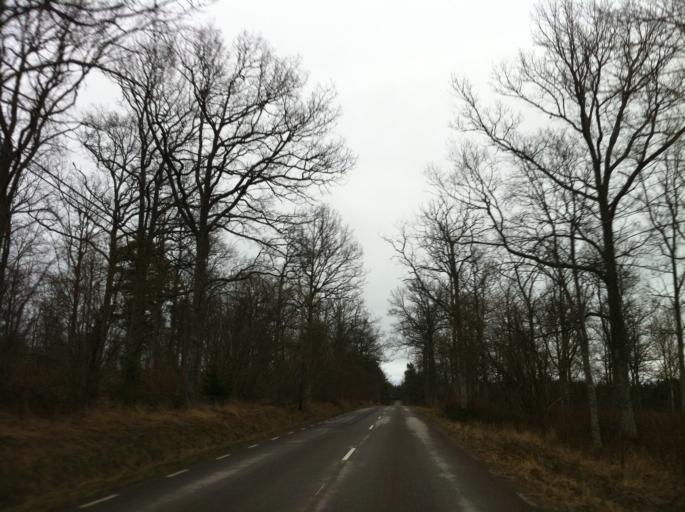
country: SE
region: Kalmar
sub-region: Vasterviks Kommun
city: Vaestervik
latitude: 57.8095
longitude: 16.5892
